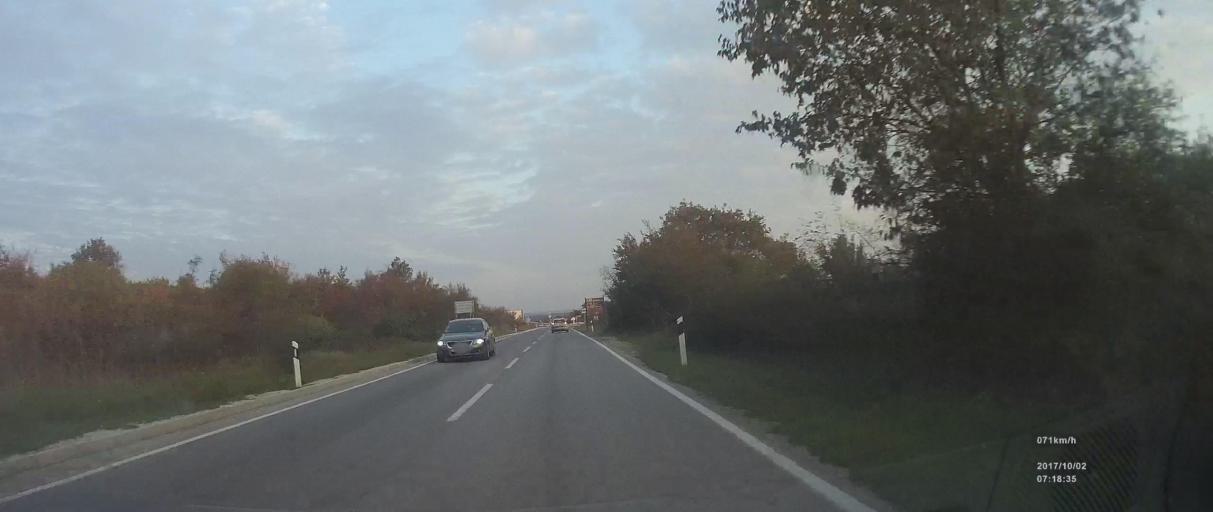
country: HR
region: Zadarska
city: Benkovac
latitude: 44.0191
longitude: 15.5929
